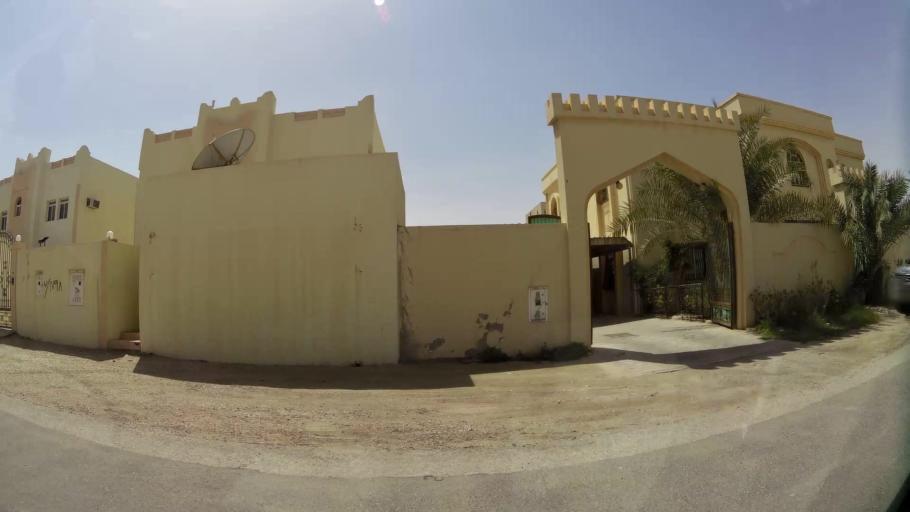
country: QA
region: Baladiyat Umm Salal
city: Umm Salal Muhammad
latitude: 25.3688
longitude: 51.4332
